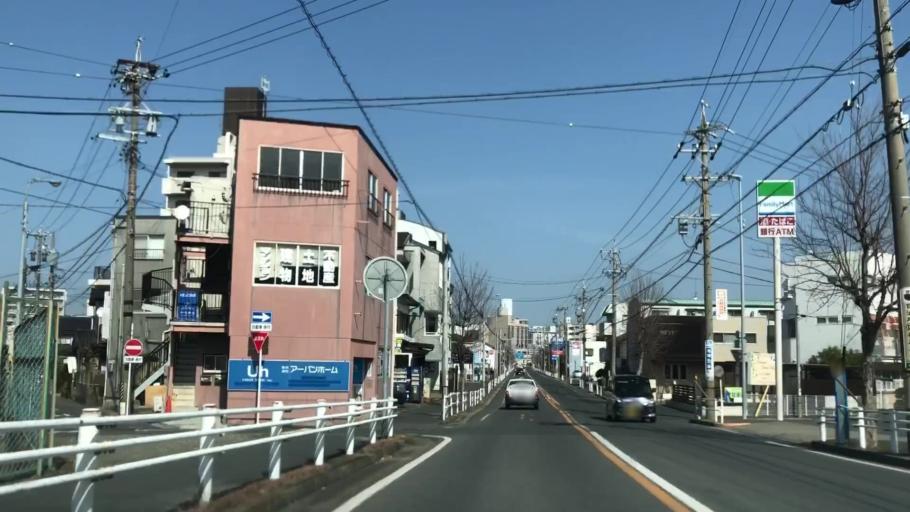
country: JP
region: Aichi
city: Toyohashi
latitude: 34.7535
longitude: 137.3792
